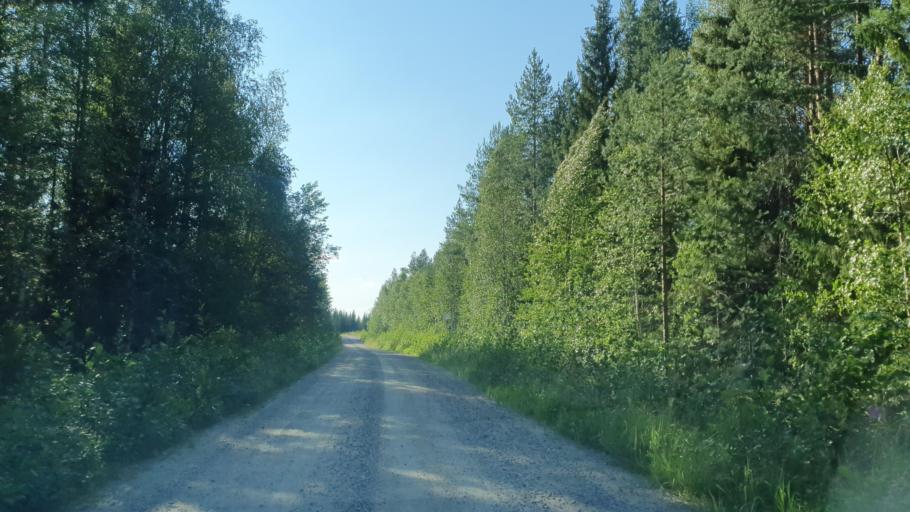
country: FI
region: Kainuu
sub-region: Kehys-Kainuu
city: Kuhmo
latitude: 64.0168
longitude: 29.7618
